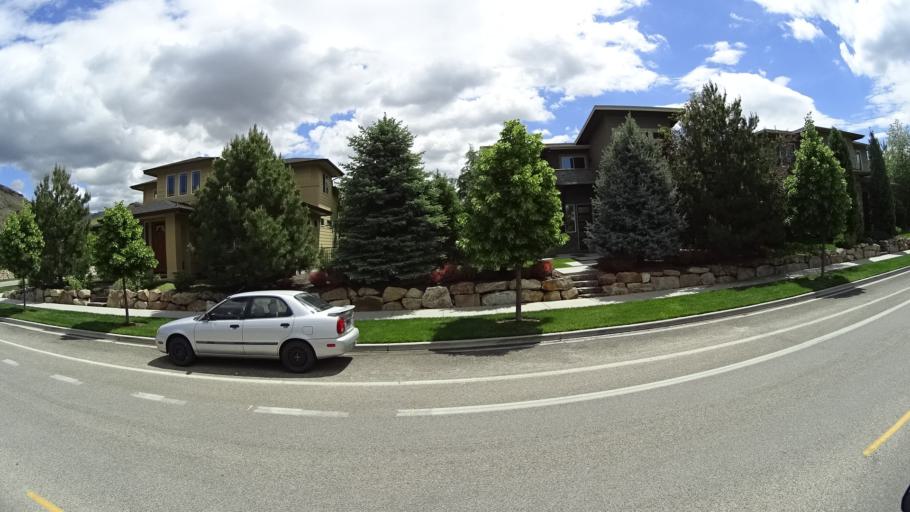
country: US
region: Idaho
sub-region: Ada County
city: Boise
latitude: 43.5790
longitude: -116.1385
